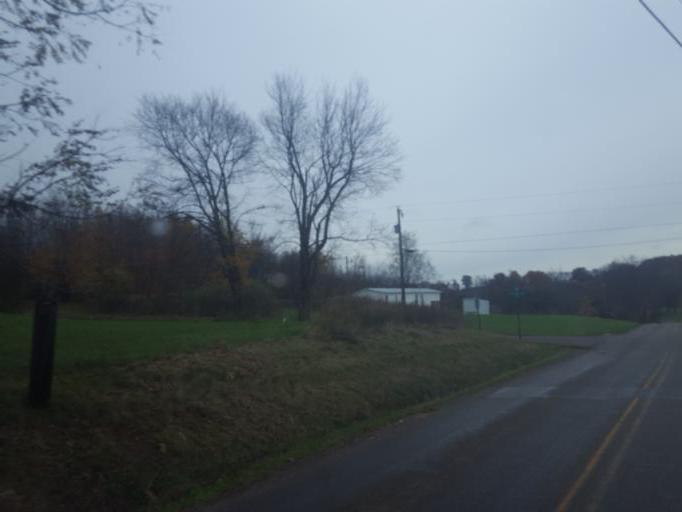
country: US
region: Ohio
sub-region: Knox County
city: Gambier
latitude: 40.4696
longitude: -82.3751
